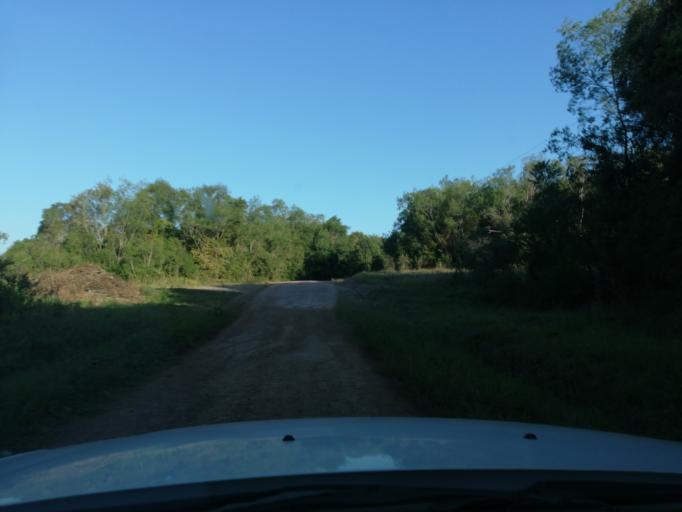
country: AR
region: Misiones
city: Cerro Cora
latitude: -27.6235
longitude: -55.7044
